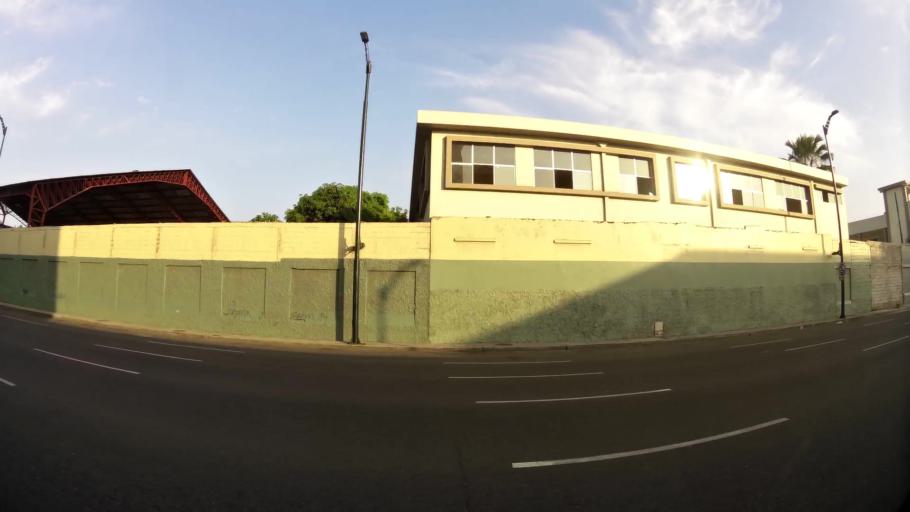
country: EC
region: Guayas
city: Guayaquil
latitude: -2.2031
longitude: -79.8938
